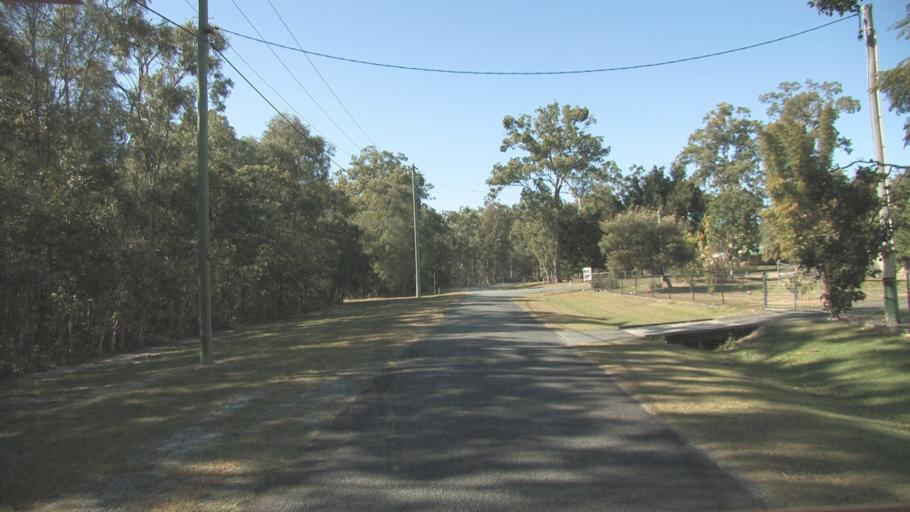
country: AU
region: Queensland
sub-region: Logan
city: Chambers Flat
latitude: -27.7820
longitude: 153.1029
